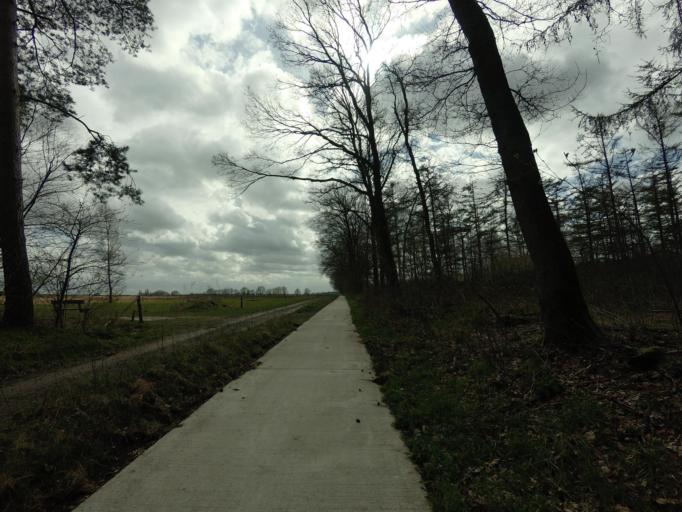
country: NL
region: Gelderland
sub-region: Gemeente Renkum
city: Heelsum
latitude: 52.0076
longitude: 5.7498
